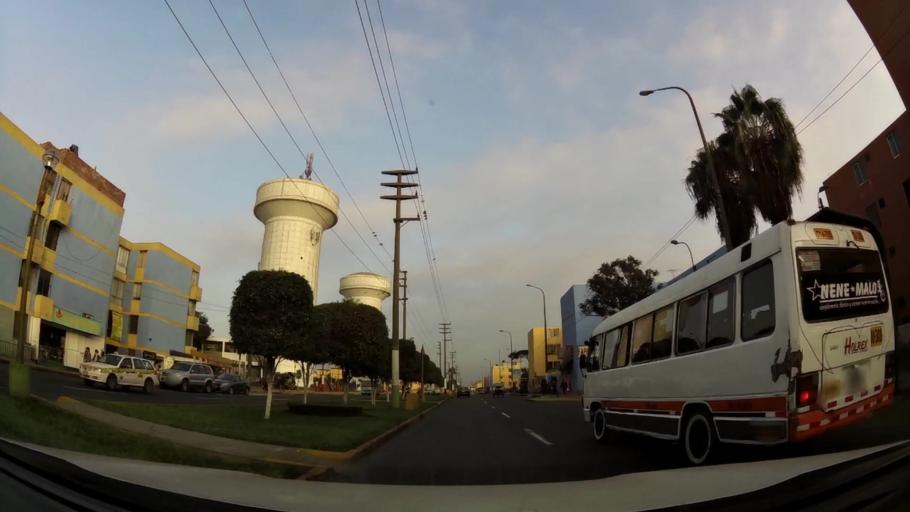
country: PE
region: Callao
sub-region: Callao
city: Callao
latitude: -12.0127
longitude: -77.1005
